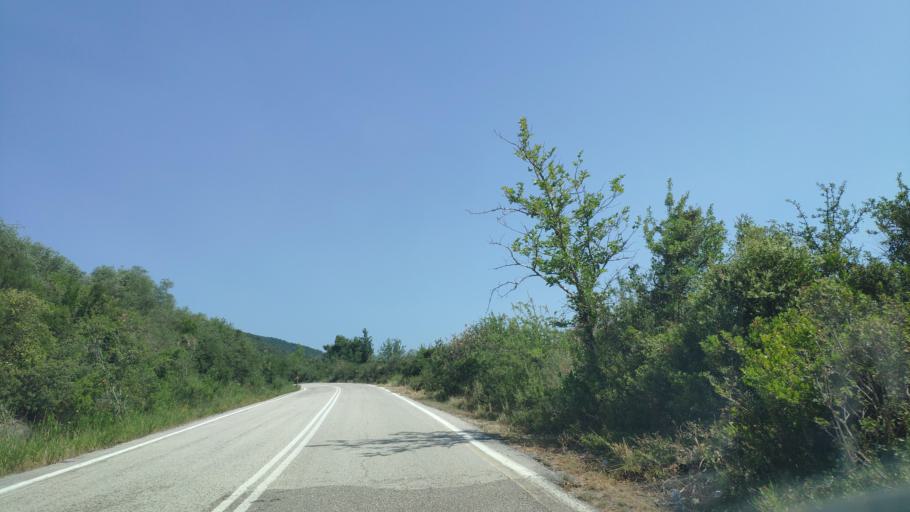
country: GR
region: West Greece
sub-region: Nomos Aitolias kai Akarnanias
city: Lepenou
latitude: 38.7553
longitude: 21.3406
